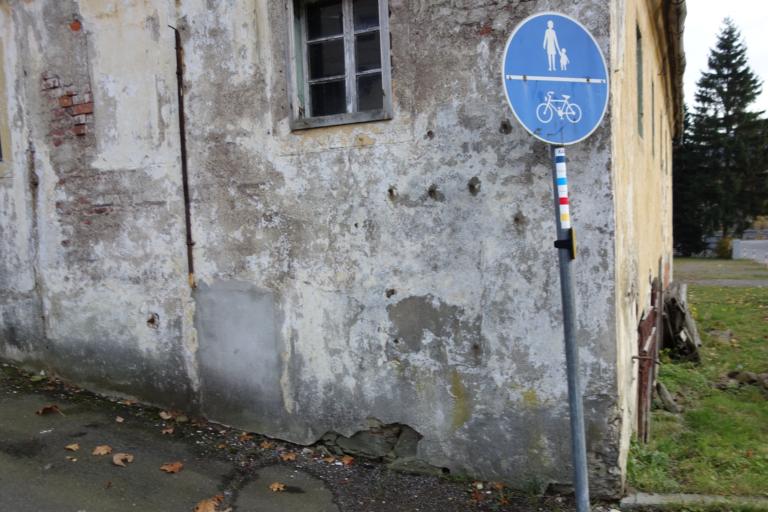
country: DE
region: Saxony
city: Olbernhau
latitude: 50.6521
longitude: 13.3695
